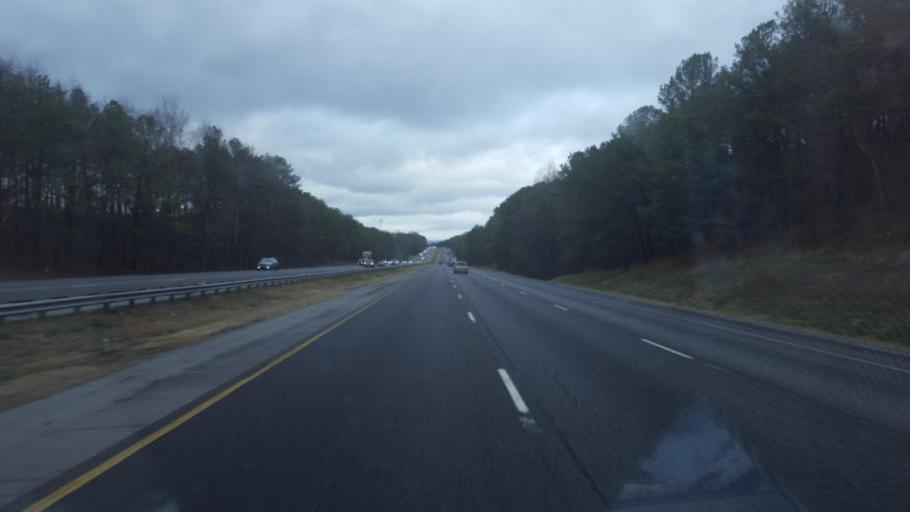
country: US
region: Georgia
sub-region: Gordon County
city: Calhoun
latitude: 34.6045
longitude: -84.9583
